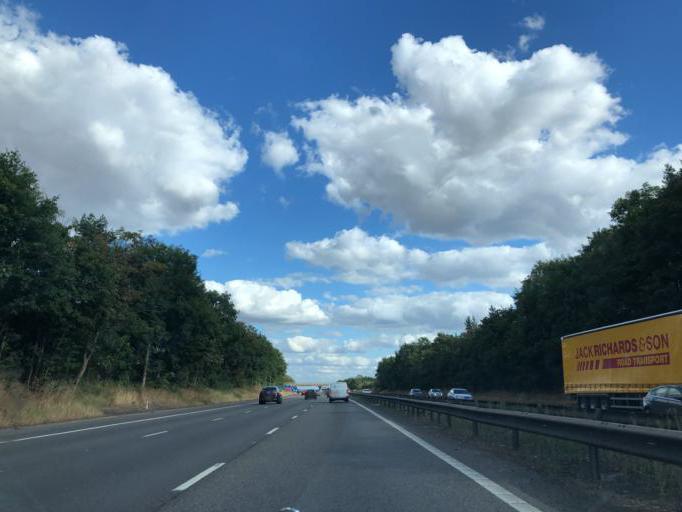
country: GB
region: England
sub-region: Milton Keynes
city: Hanslope
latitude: 52.1342
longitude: -0.8278
